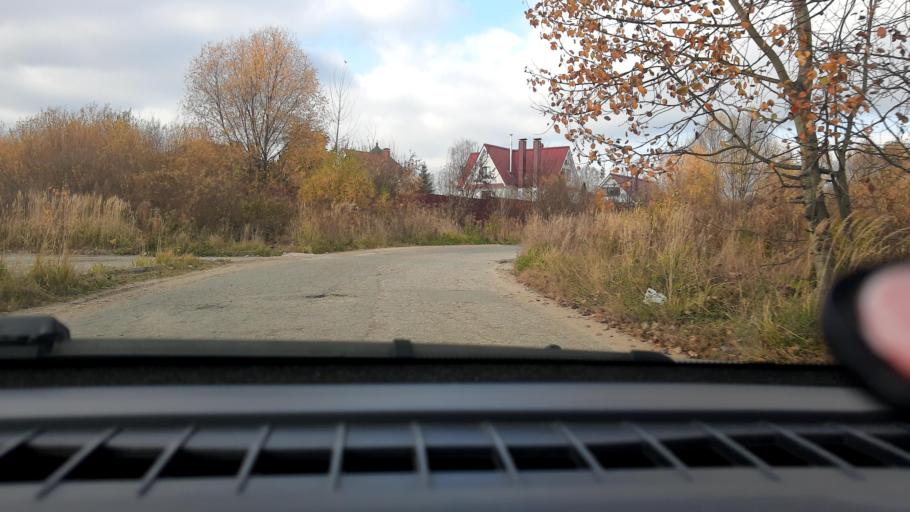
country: RU
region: Nizjnij Novgorod
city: Afonino
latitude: 56.1994
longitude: 44.0961
